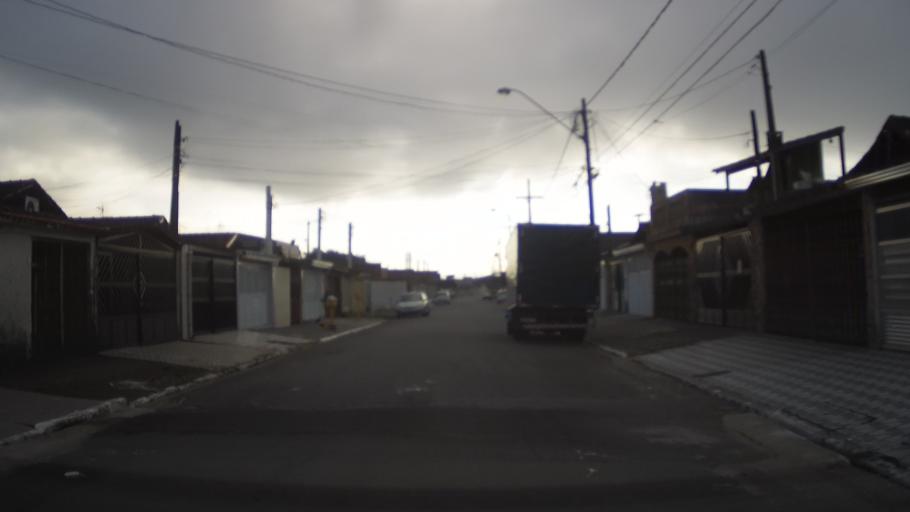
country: BR
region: Sao Paulo
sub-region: Praia Grande
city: Praia Grande
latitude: -24.0153
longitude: -46.4685
